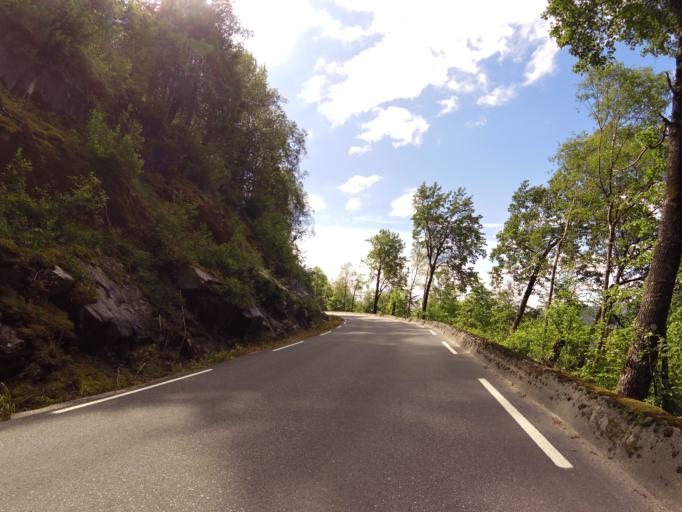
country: NO
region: Vest-Agder
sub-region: Kvinesdal
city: Liknes
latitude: 58.2928
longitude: 6.9424
